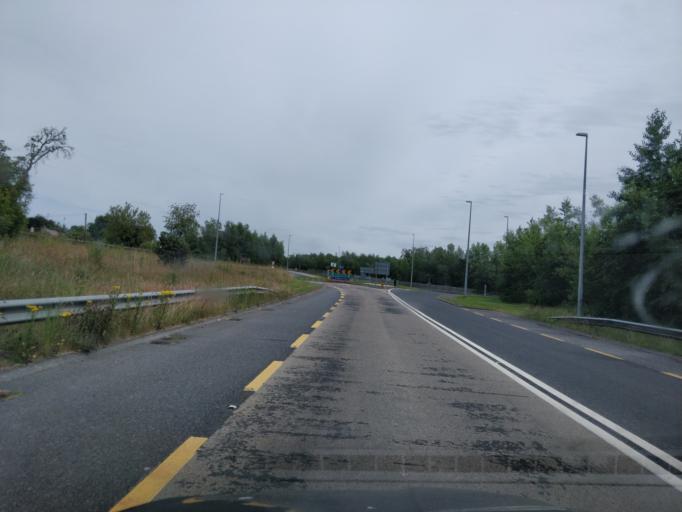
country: IE
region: Leinster
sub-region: Uibh Fhaili
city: Tullamore
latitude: 53.2519
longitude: -7.5166
